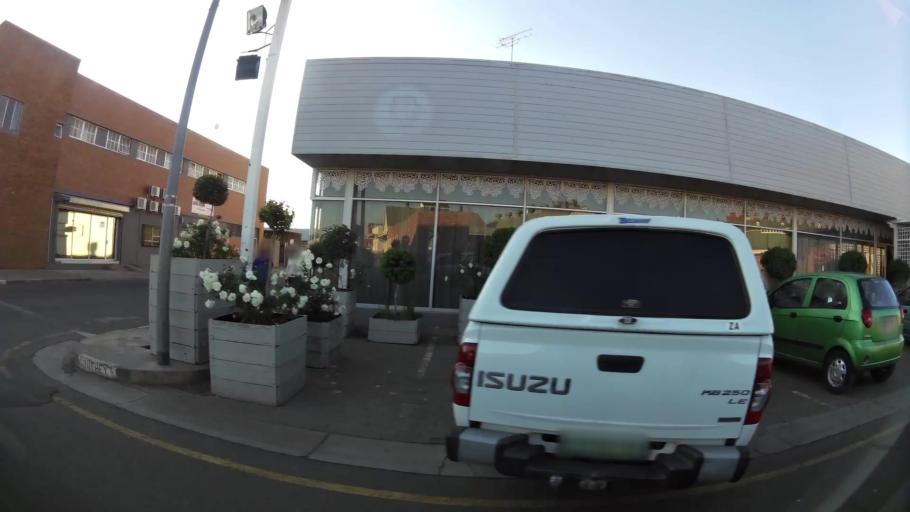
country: ZA
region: Northern Cape
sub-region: Frances Baard District Municipality
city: Kimberley
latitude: -28.7375
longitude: 24.7616
